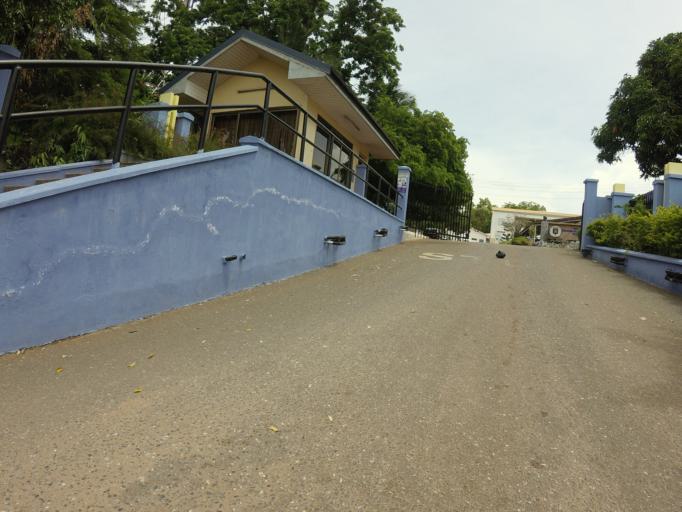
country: GH
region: Greater Accra
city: Accra
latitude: 5.5966
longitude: -0.2228
